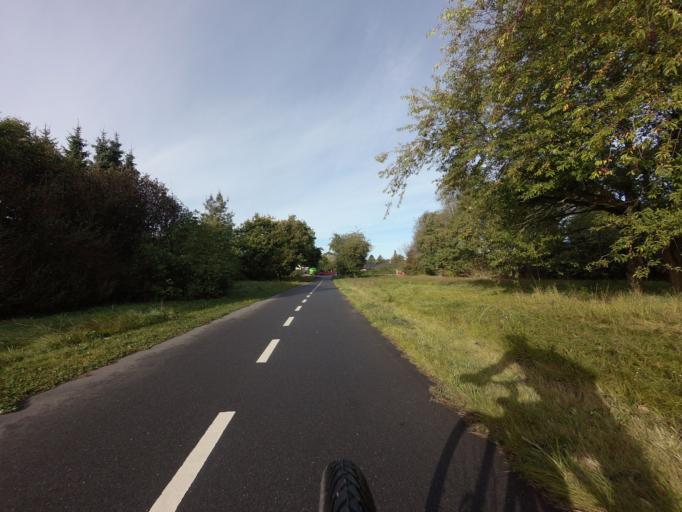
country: DK
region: Central Jutland
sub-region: Viborg Kommune
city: Viborg
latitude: 56.4216
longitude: 9.4431
